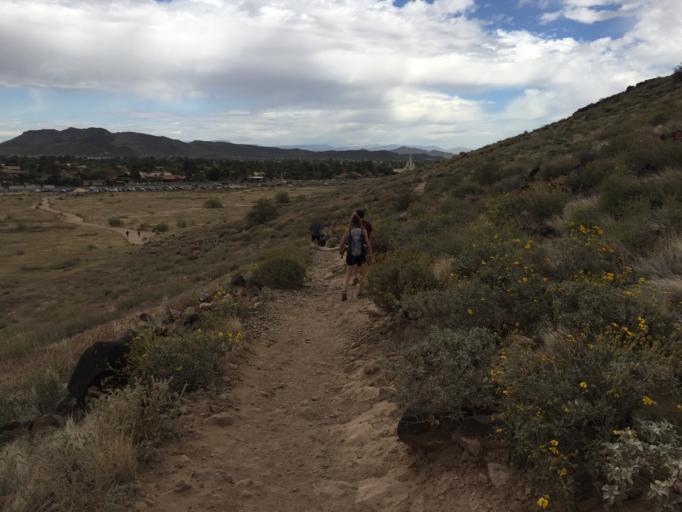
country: US
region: Arizona
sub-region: Maricopa County
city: Peoria
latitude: 33.6942
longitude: -112.1796
